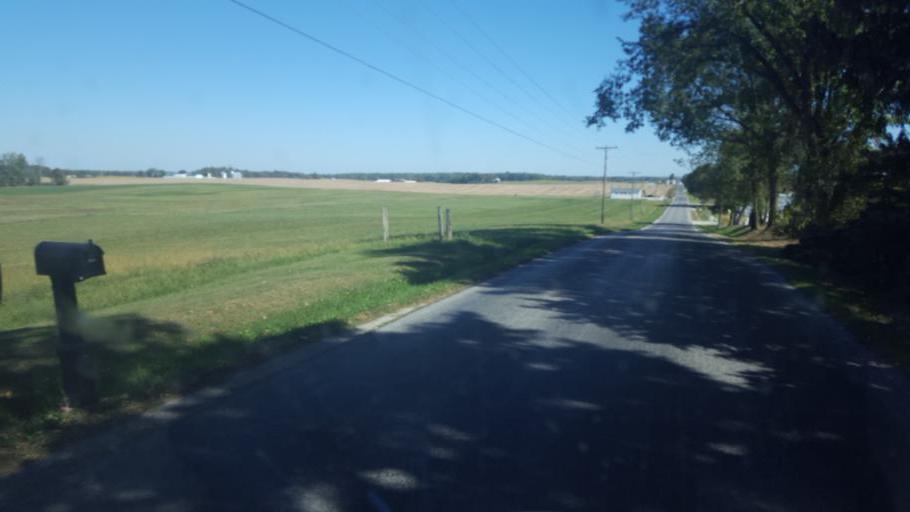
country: US
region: Ohio
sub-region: Huron County
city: Greenwich
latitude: 40.9929
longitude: -82.4715
